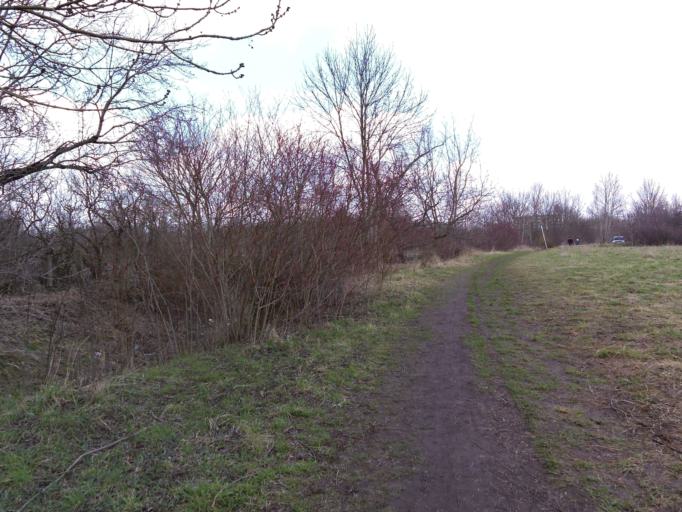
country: DE
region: Saxony
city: Markranstadt
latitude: 51.3065
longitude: 12.2567
